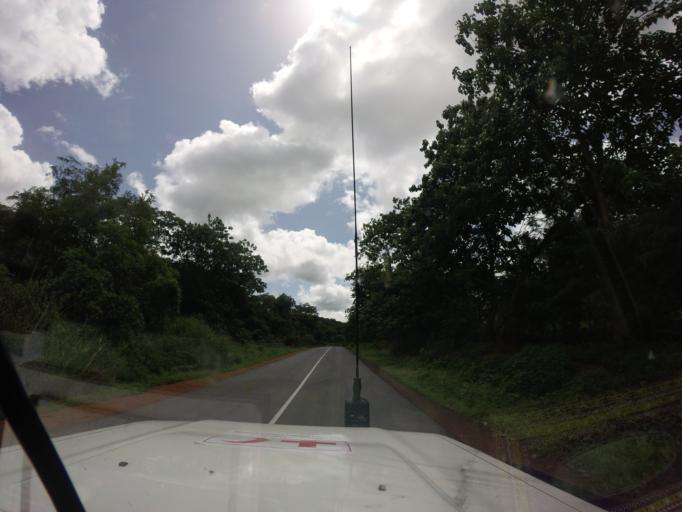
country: SL
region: Northern Province
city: Bindi
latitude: 10.1564
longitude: -11.6911
